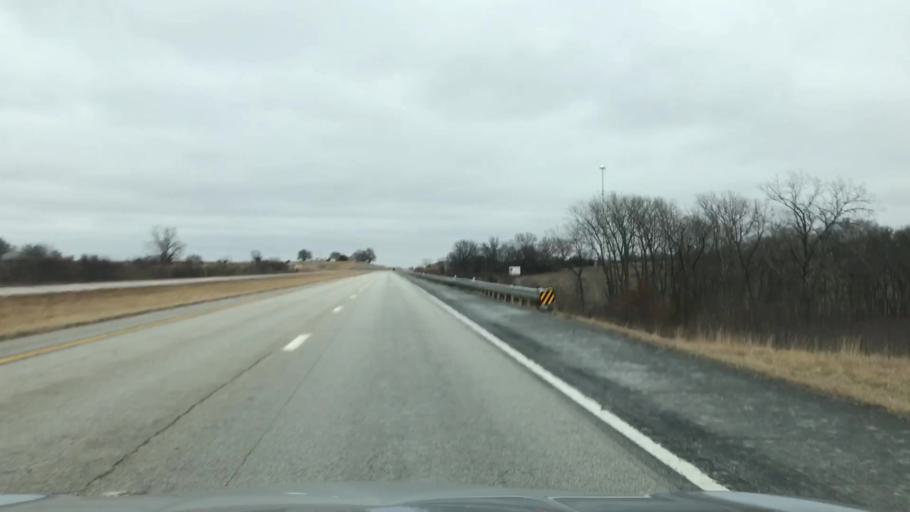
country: US
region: Missouri
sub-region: Caldwell County
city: Hamilton
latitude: 39.7490
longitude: -94.0626
